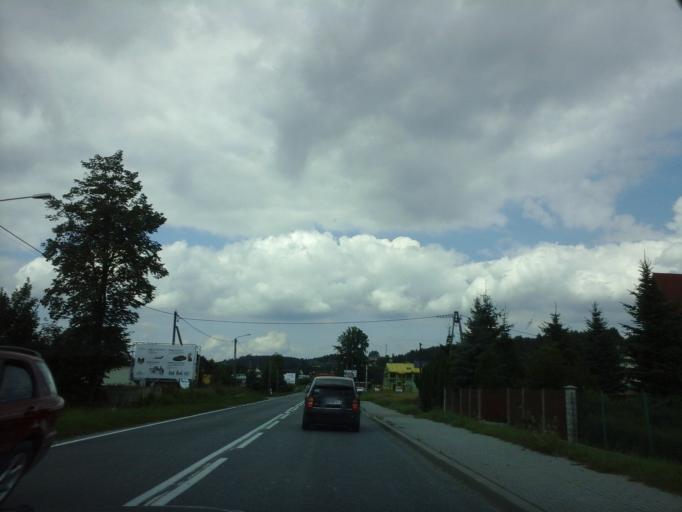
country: PL
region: Lesser Poland Voivodeship
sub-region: Powiat suski
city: Jordanow
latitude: 49.6555
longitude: 19.8143
